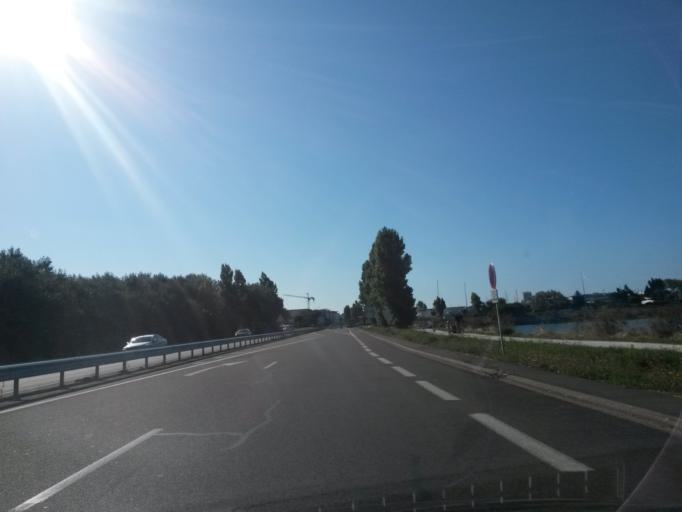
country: FR
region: Pays de la Loire
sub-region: Departement de la Vendee
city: Les Sables-d'Olonne
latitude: 46.5070
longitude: -1.7917
